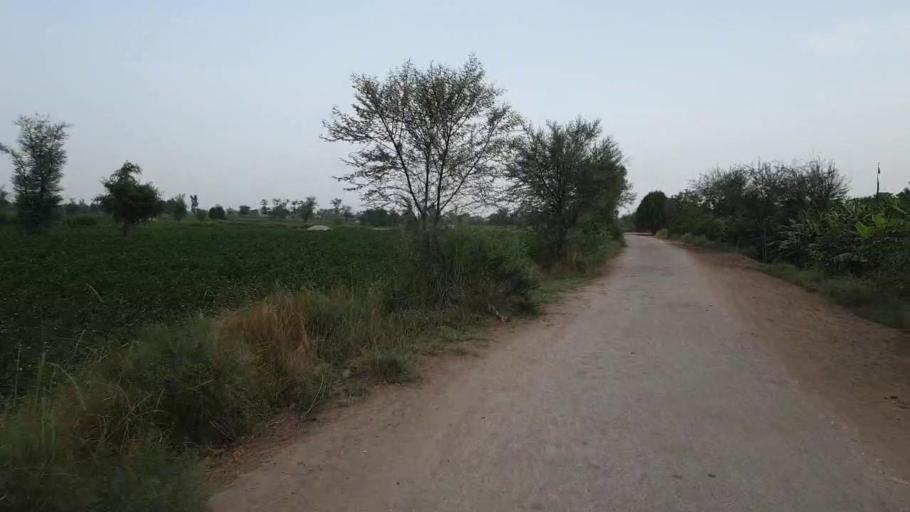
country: PK
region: Sindh
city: Bandhi
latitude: 26.5333
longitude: 68.2042
